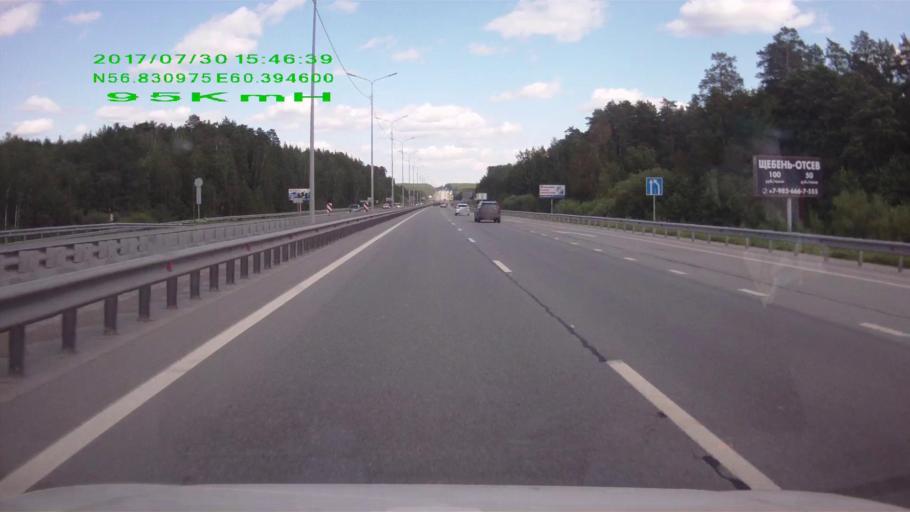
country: RU
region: Sverdlovsk
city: Shirokaya Rechka
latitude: 56.8309
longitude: 60.3952
